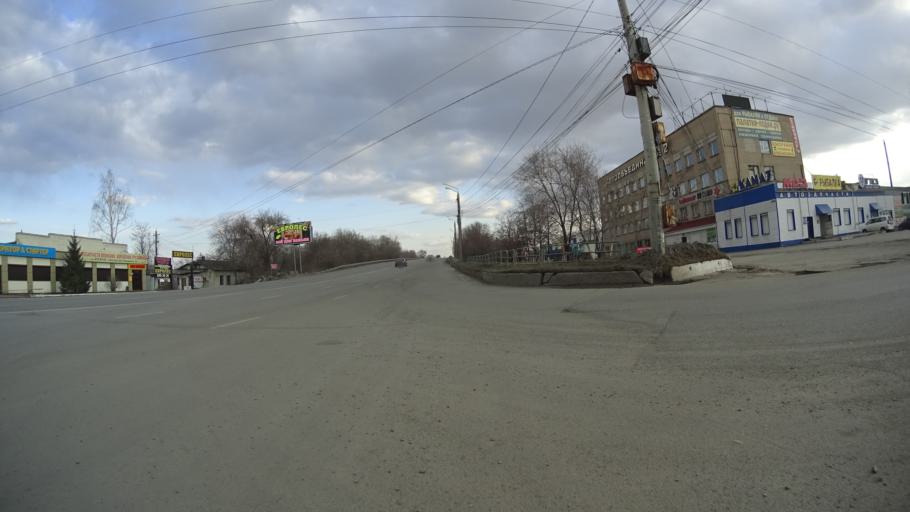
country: RU
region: Chelyabinsk
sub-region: Gorod Chelyabinsk
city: Chelyabinsk
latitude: 55.1055
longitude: 61.3871
